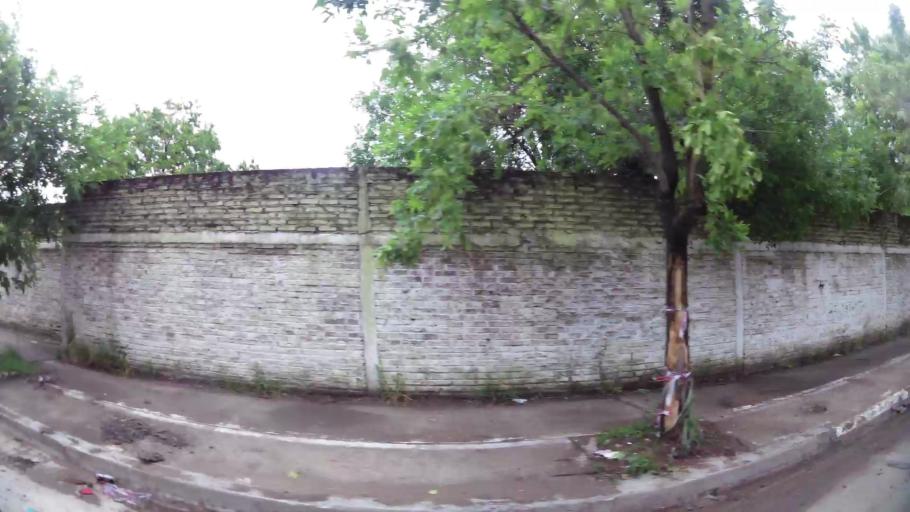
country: AR
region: Buenos Aires
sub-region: Partido de Lanus
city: Lanus
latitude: -34.7338
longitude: -58.3759
